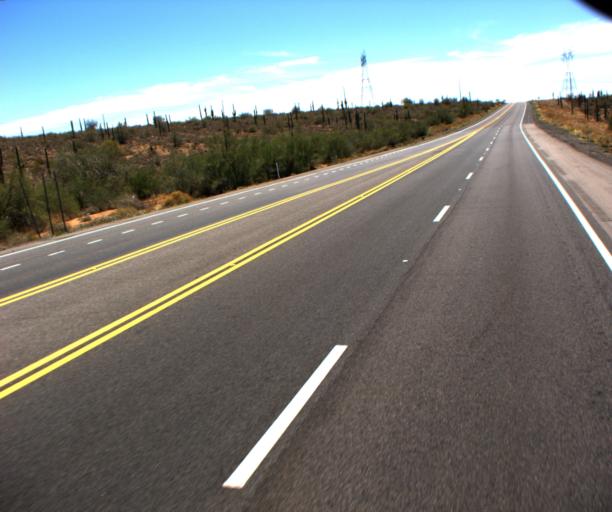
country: US
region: Arizona
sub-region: Maricopa County
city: Anthem
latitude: 33.8247
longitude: -112.2583
